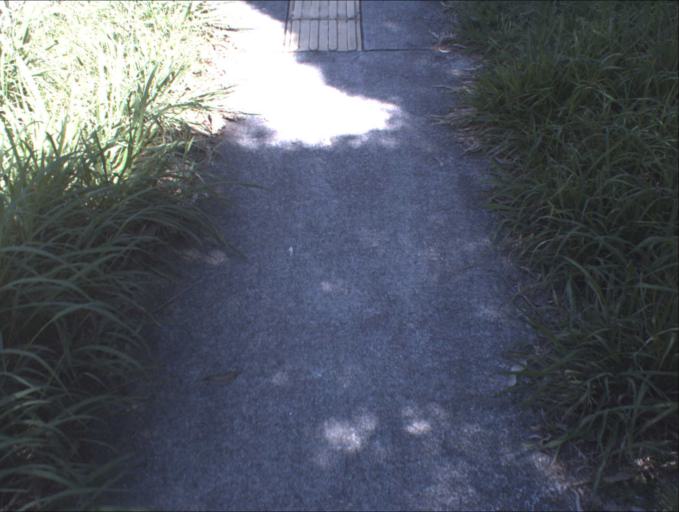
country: AU
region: Queensland
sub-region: Logan
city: Beenleigh
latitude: -27.7069
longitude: 153.1818
